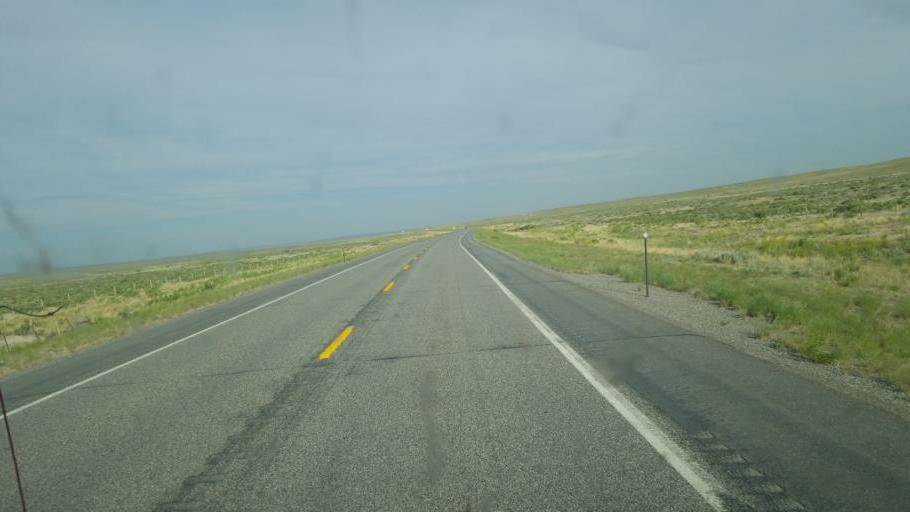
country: US
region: Wyoming
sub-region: Fremont County
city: Riverton
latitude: 43.1622
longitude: -107.7356
